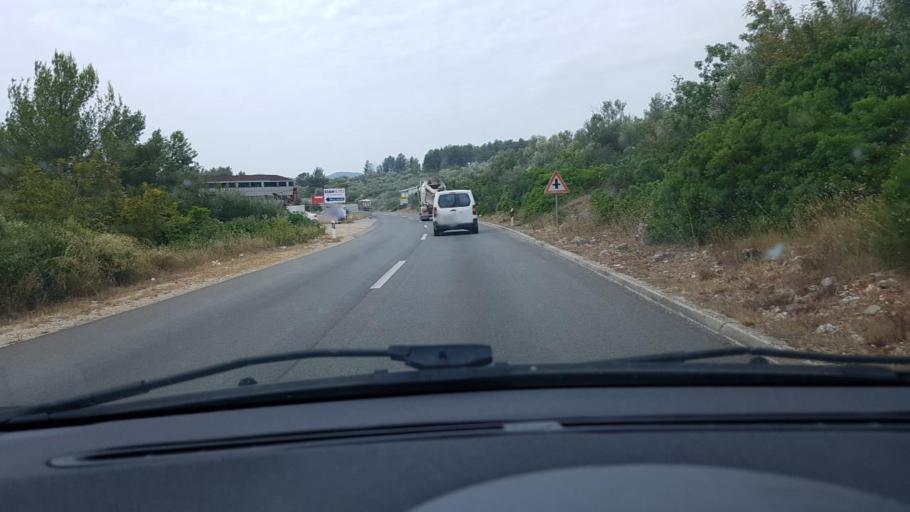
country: HR
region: Dubrovacko-Neretvanska
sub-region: Grad Dubrovnik
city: Vela Luka
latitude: 42.9483
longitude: 16.7709
